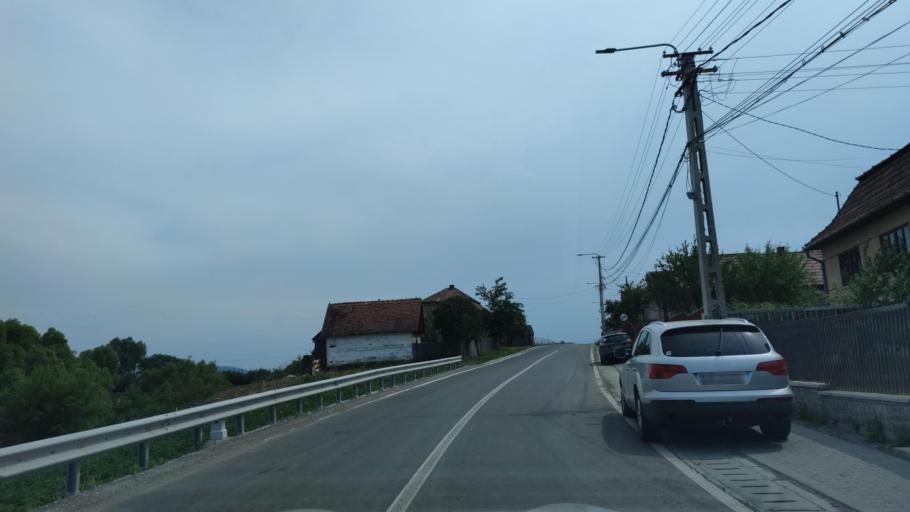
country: RO
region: Harghita
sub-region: Comuna Remetea
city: Remetea
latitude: 46.8103
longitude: 25.4594
